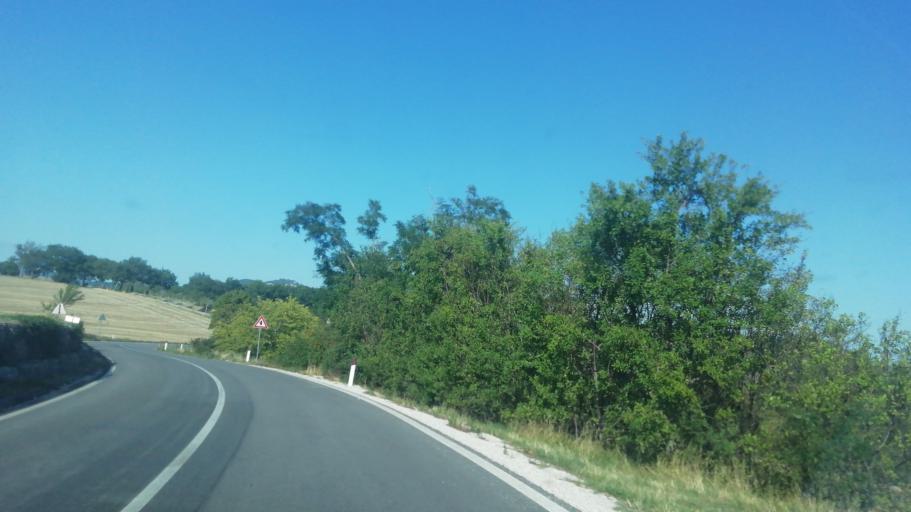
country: IT
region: The Marches
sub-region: Provincia di Pesaro e Urbino
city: Frontone
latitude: 43.5375
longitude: 12.7378
